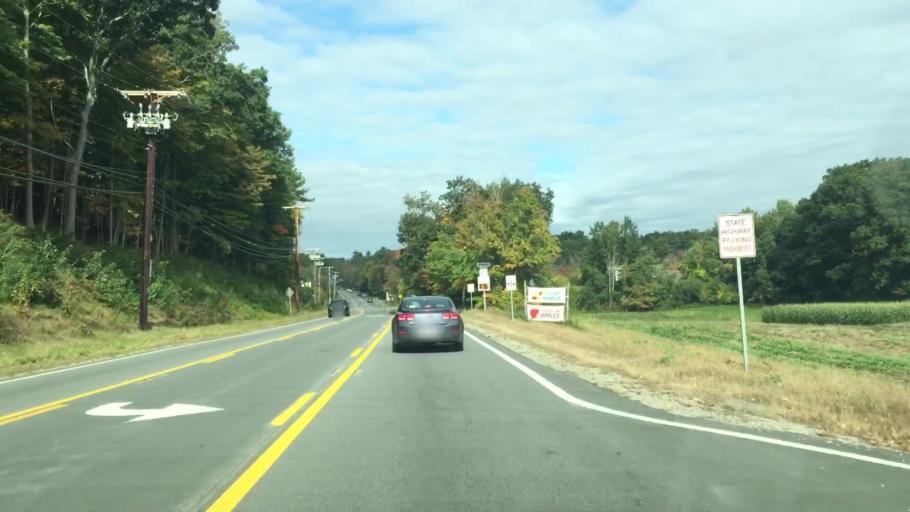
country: US
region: Massachusetts
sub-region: Essex County
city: Andover
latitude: 42.6471
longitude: -71.0900
